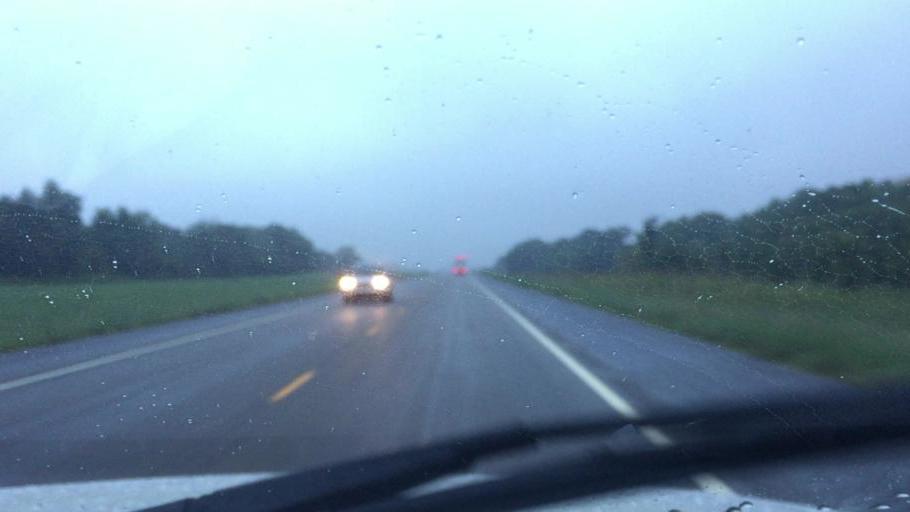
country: US
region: Kansas
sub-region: Montgomery County
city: Cherryvale
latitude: 37.4126
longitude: -95.4984
